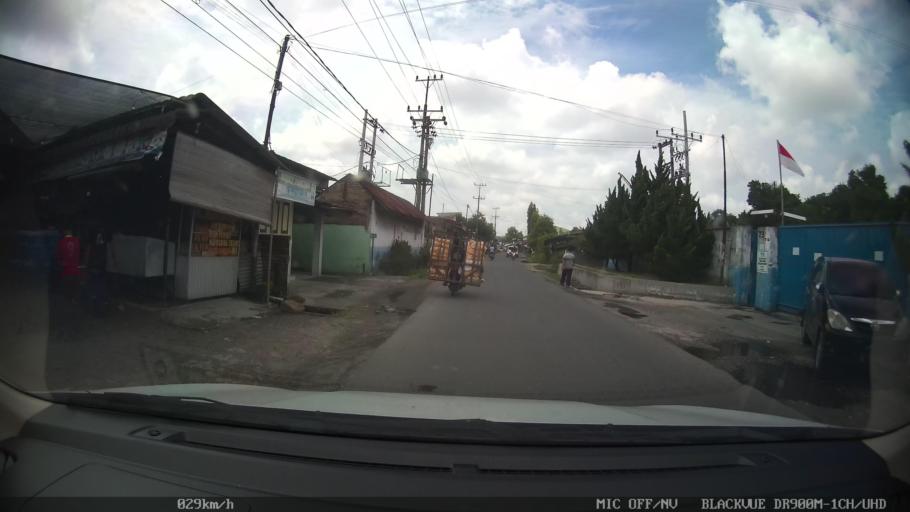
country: ID
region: North Sumatra
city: Medan
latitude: 3.6068
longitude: 98.7475
